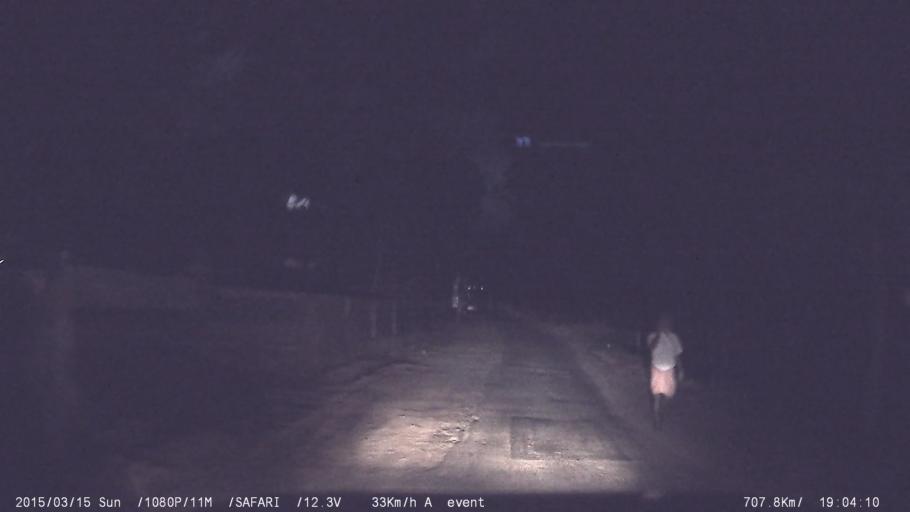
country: IN
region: Kerala
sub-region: Ernakulam
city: Muvattupuzha
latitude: 9.8819
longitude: 76.6435
